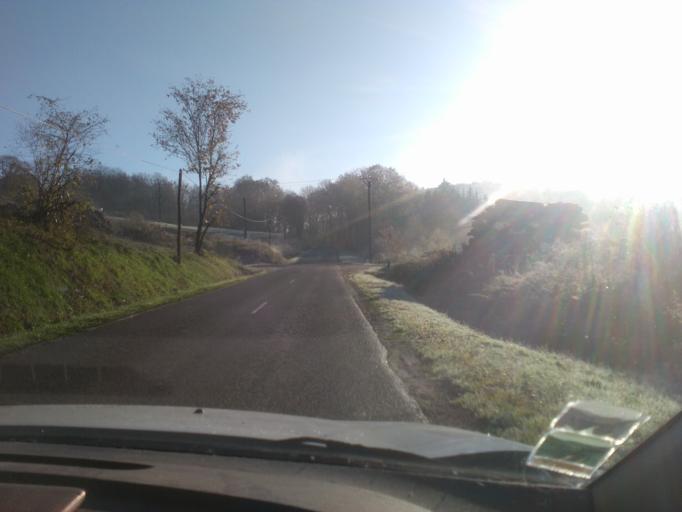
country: FR
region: Lorraine
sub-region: Departement des Vosges
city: Uzemain
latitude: 48.0592
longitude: 6.3423
